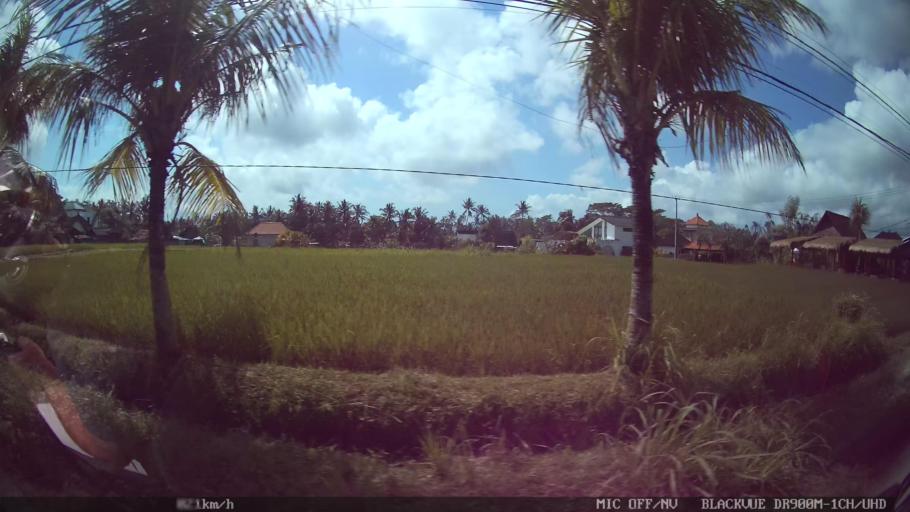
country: ID
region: Bali
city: Banjar Tebongkang
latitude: -8.5516
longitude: 115.2749
